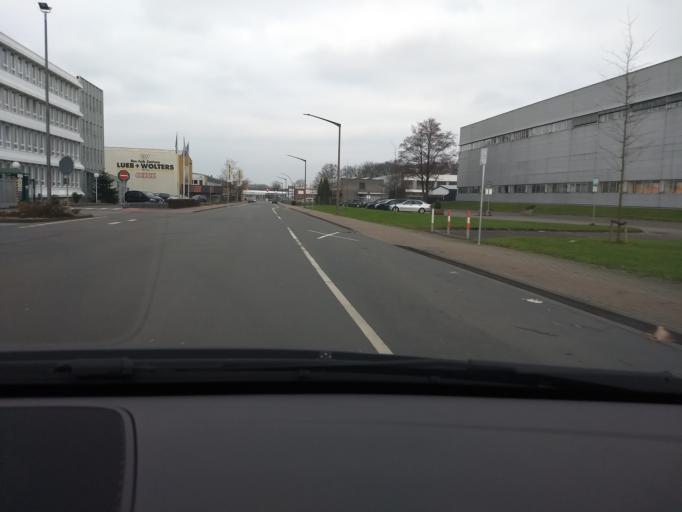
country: DE
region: North Rhine-Westphalia
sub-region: Regierungsbezirk Munster
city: Borken
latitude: 51.8483
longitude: 6.8719
